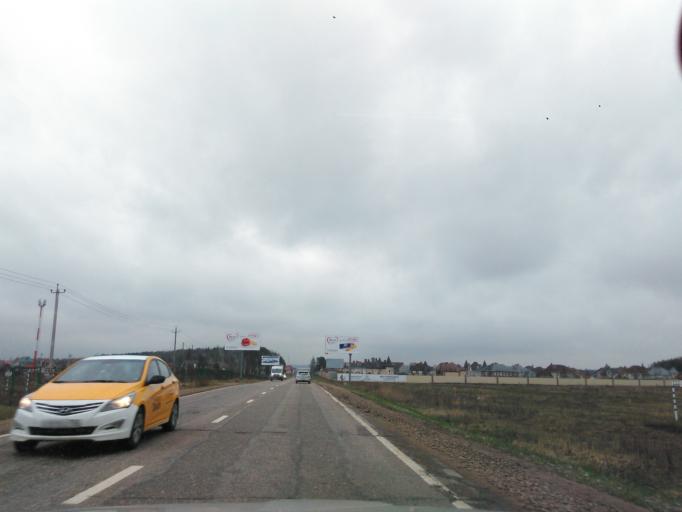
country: RU
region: Moskovskaya
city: Rozhdestveno
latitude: 55.8289
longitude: 37.0343
